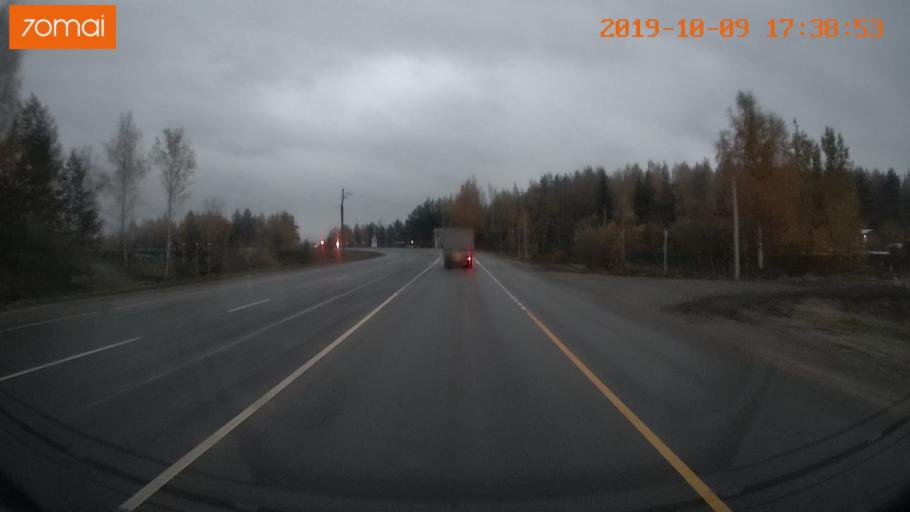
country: RU
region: Ivanovo
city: Bogorodskoye
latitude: 57.0660
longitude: 40.9526
